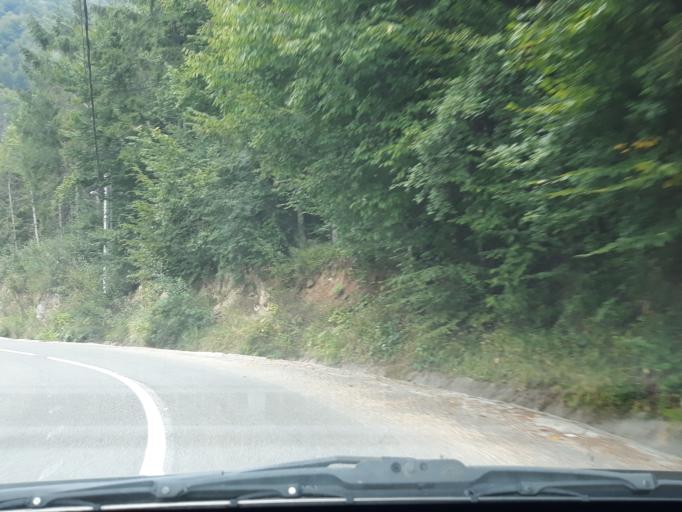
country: RO
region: Bihor
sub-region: Comuna Pietroasa
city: Pietroasa
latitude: 46.6032
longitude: 22.6467
